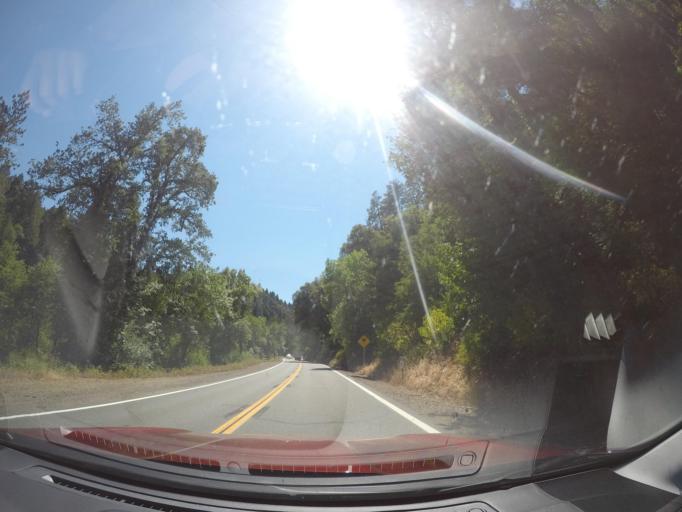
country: US
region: California
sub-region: Shasta County
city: Bella Vista
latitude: 40.7509
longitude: -122.0476
